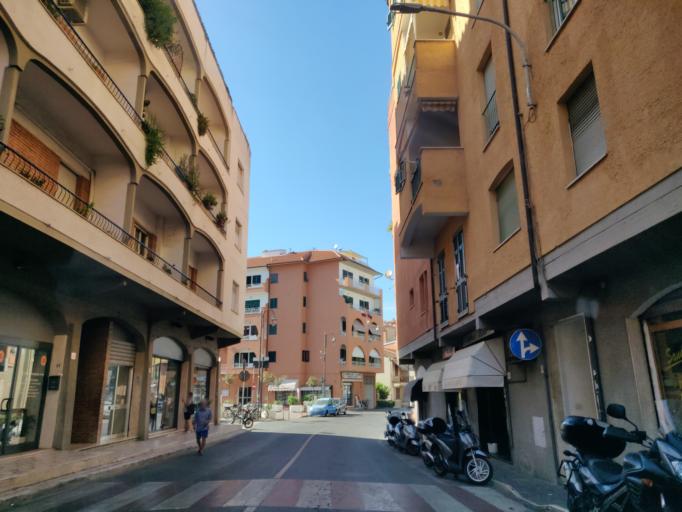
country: IT
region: Tuscany
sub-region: Provincia di Grosseto
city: Porto Ercole
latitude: 42.3932
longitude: 11.2044
